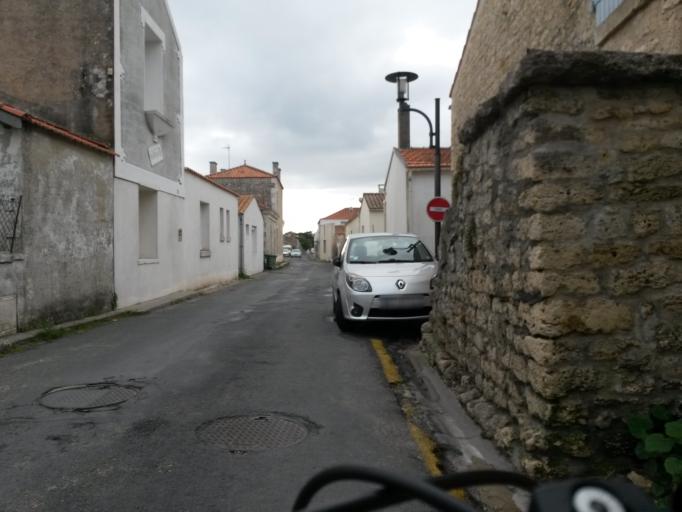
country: FR
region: Poitou-Charentes
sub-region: Departement de la Charente-Maritime
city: Dolus-d'Oleron
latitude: 45.9187
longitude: -1.3346
